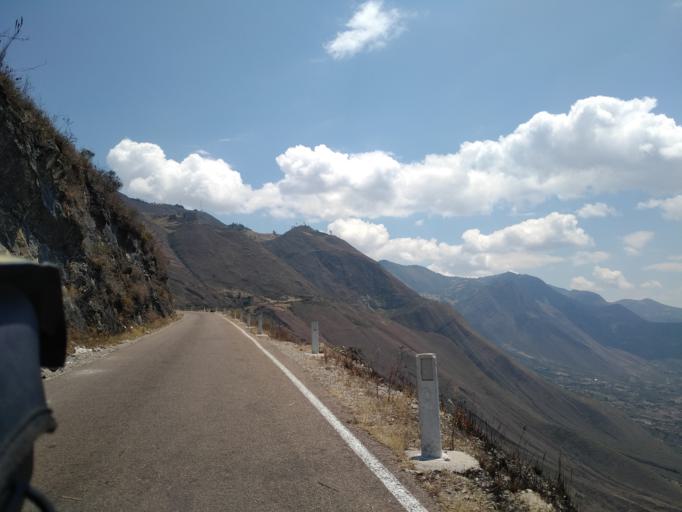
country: PE
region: Cajamarca
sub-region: Provincia de Celendin
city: Utco
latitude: -6.8892
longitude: -78.0964
